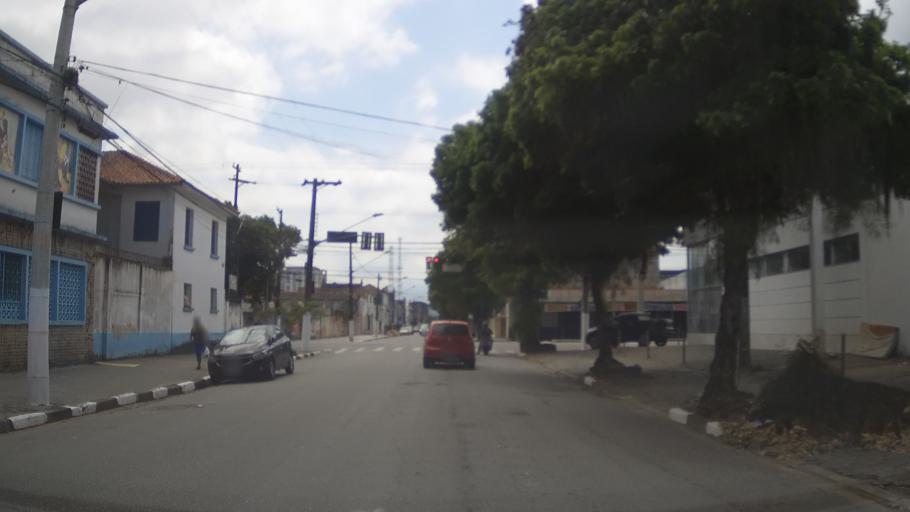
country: BR
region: Sao Paulo
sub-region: Santos
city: Santos
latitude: -23.9567
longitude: -46.3187
